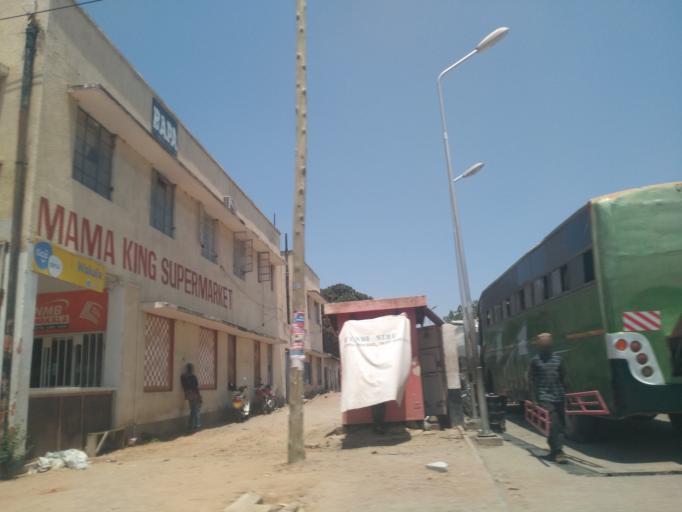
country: TZ
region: Dodoma
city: Dodoma
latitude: -6.1776
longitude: 35.7470
